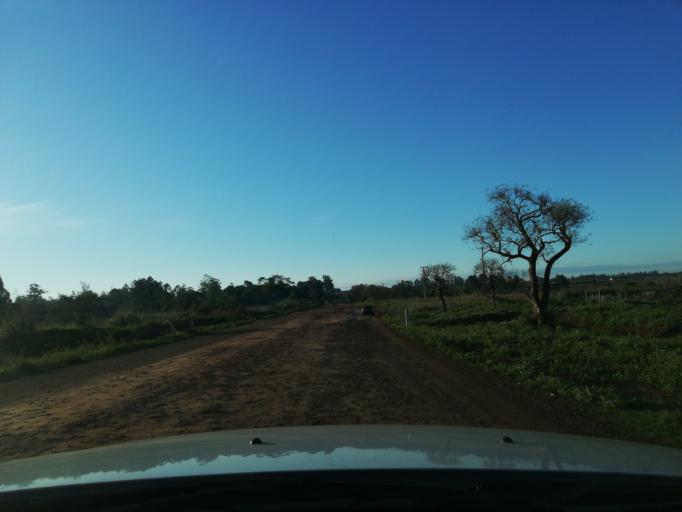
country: AR
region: Misiones
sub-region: Departamento de Capital
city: Posadas
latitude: -27.4713
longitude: -55.9708
